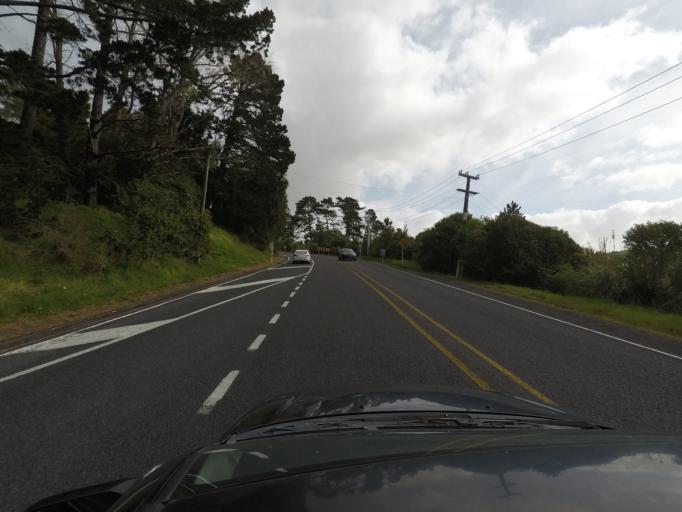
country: NZ
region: Auckland
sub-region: Auckland
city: Pakuranga
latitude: -36.9265
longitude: 174.9357
